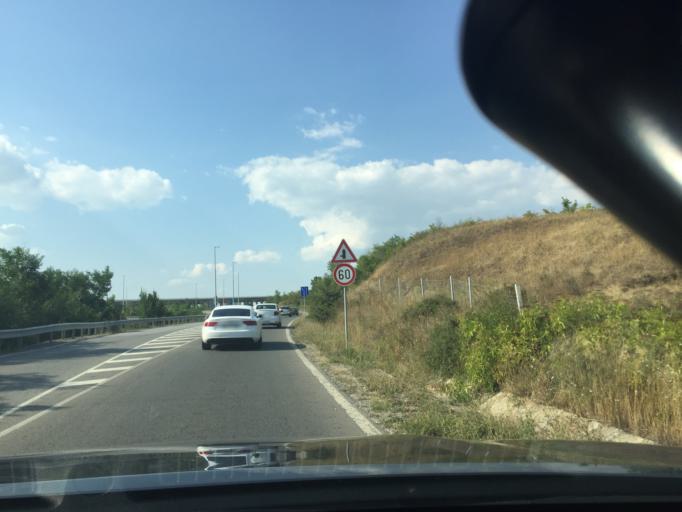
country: BG
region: Kyustendil
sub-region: Obshtina Dupnitsa
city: Dupnitsa
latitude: 42.2639
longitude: 23.0719
